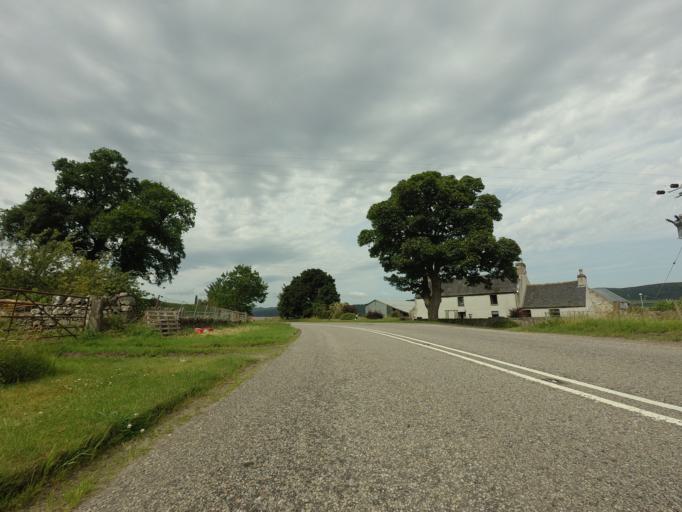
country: GB
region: Scotland
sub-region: Highland
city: Alness
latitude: 57.8583
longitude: -4.3124
